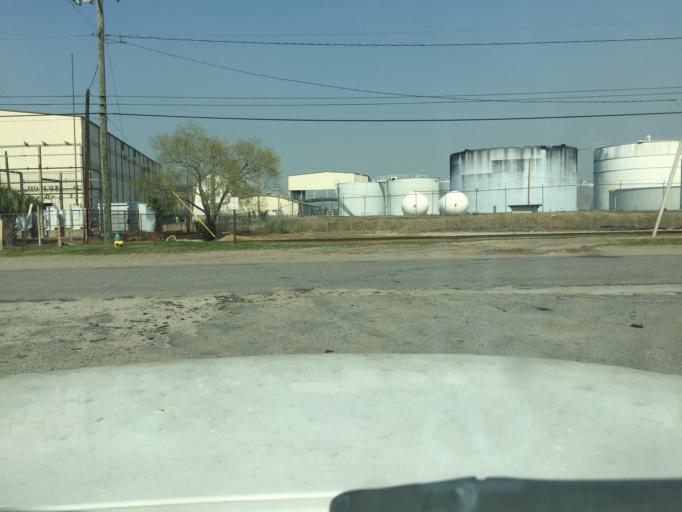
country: US
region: Georgia
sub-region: Chatham County
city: Savannah
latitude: 32.0947
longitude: -81.1135
